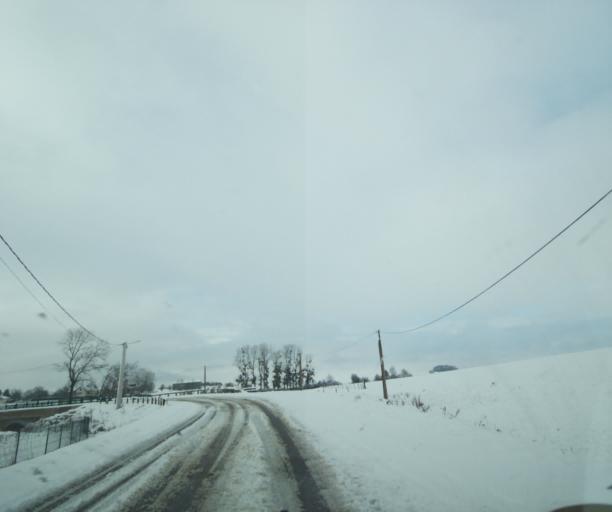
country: FR
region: Champagne-Ardenne
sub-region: Departement de la Haute-Marne
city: Montier-en-Der
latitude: 48.5243
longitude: 4.7070
